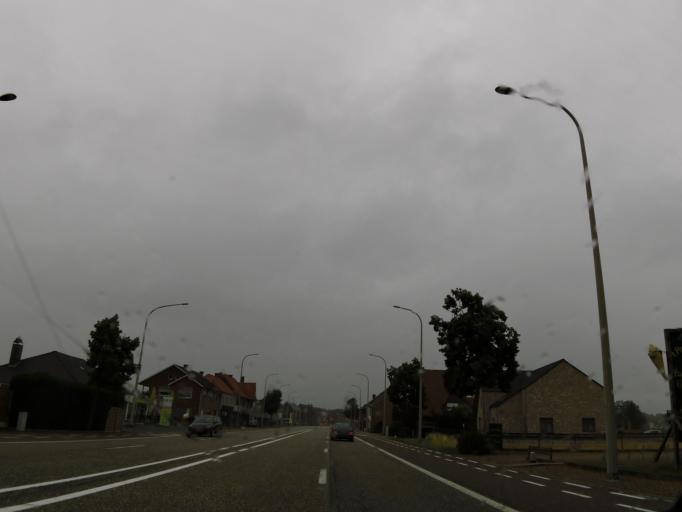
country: NL
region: Limburg
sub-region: Gemeente Stein
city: Berg
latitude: 51.0302
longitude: 5.7276
